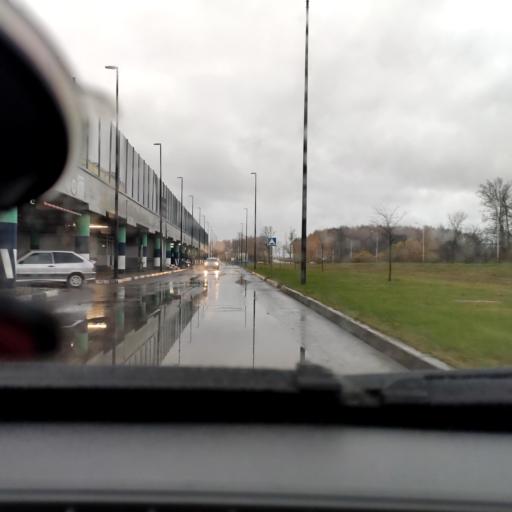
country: RU
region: Bashkortostan
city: Ufa
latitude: 54.6751
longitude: 55.9263
